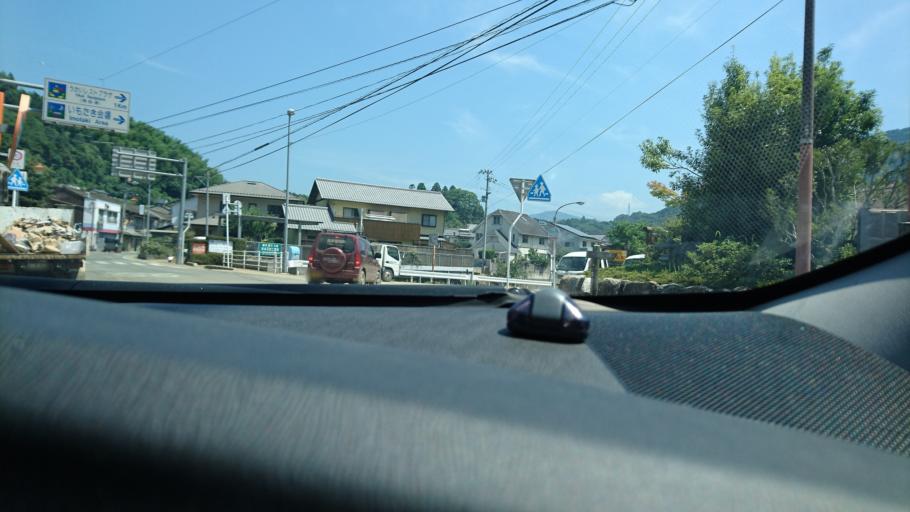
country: JP
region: Ehime
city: Ozu
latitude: 33.5026
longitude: 132.5488
